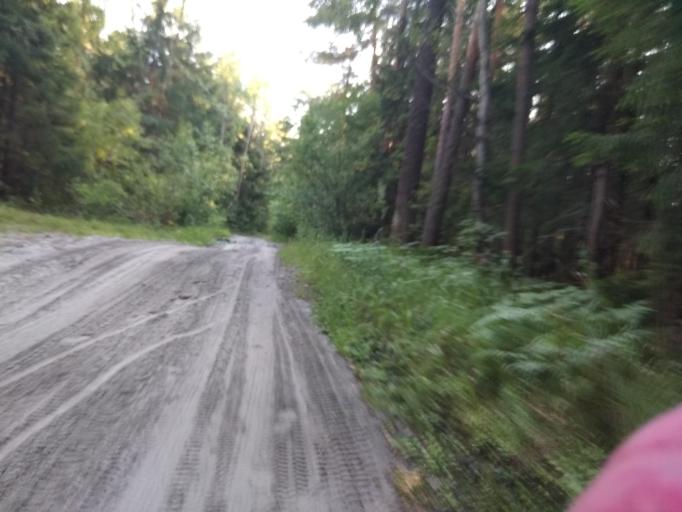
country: RU
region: Moskovskaya
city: Misheronskiy
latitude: 55.7274
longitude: 39.7583
